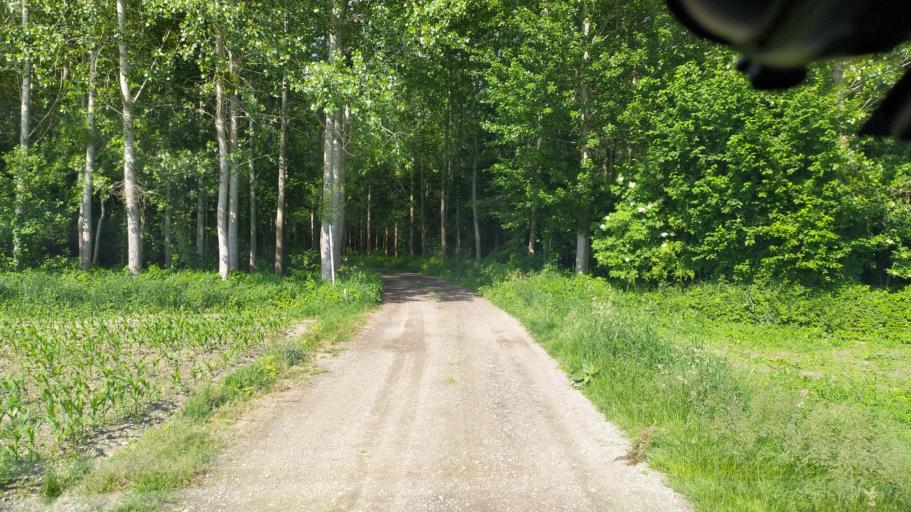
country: AT
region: Lower Austria
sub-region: Politischer Bezirk Amstetten
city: Strengberg
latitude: 48.1729
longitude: 14.6871
